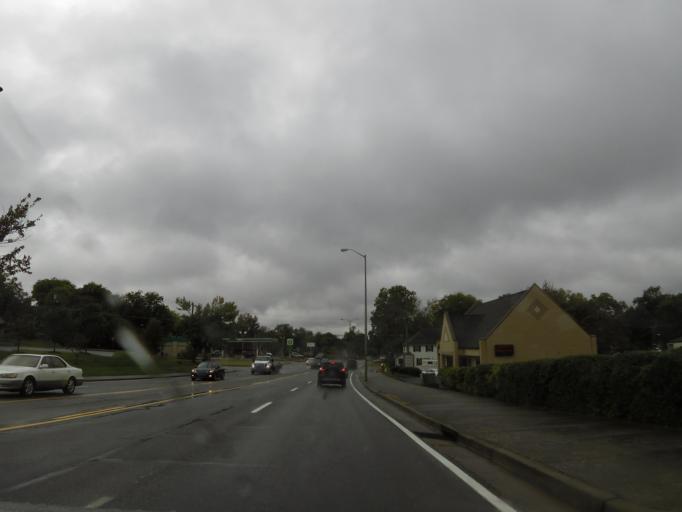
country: US
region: Tennessee
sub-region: Blount County
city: Maryville
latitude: 35.7511
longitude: -83.9788
